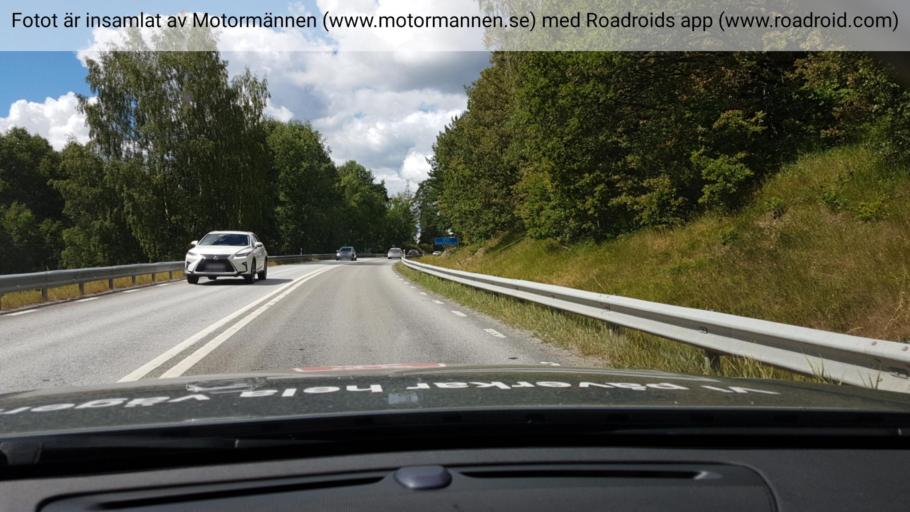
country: SE
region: Stockholm
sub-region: Vaxholms Kommun
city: Resaro
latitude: 59.4179
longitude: 18.3069
